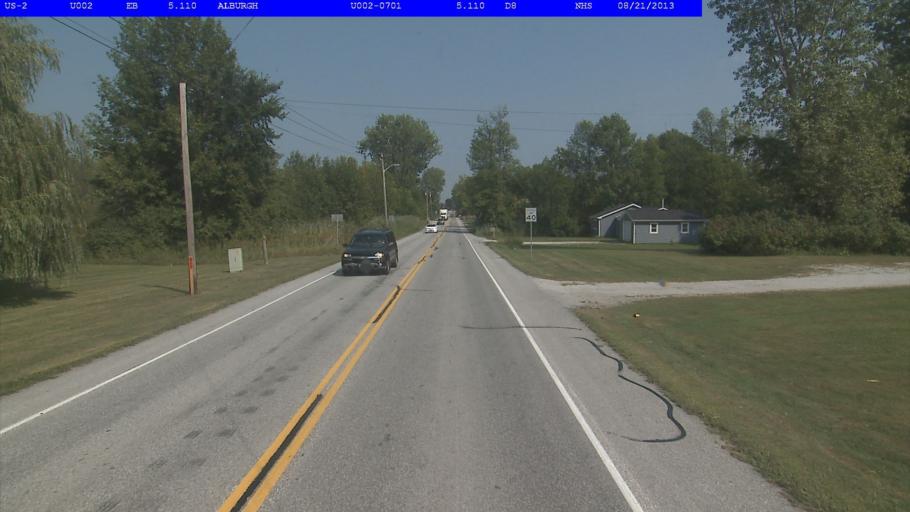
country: US
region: New York
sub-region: Clinton County
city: Rouses Point
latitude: 44.9652
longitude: -73.2962
